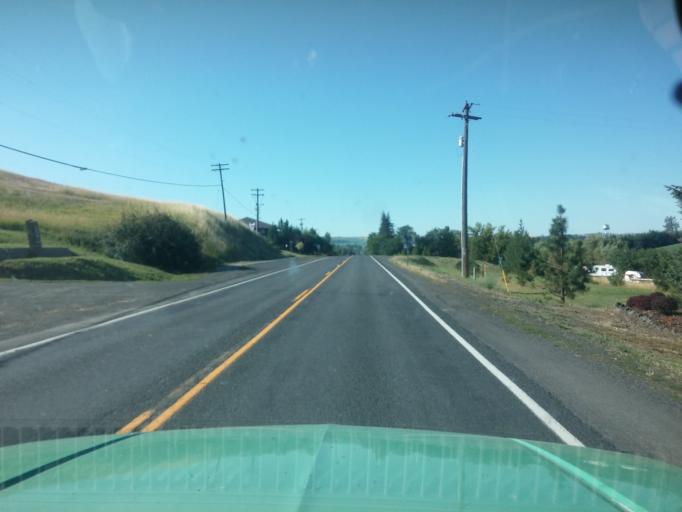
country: US
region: Idaho
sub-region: Latah County
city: Moscow
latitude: 46.7487
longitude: -117.0016
